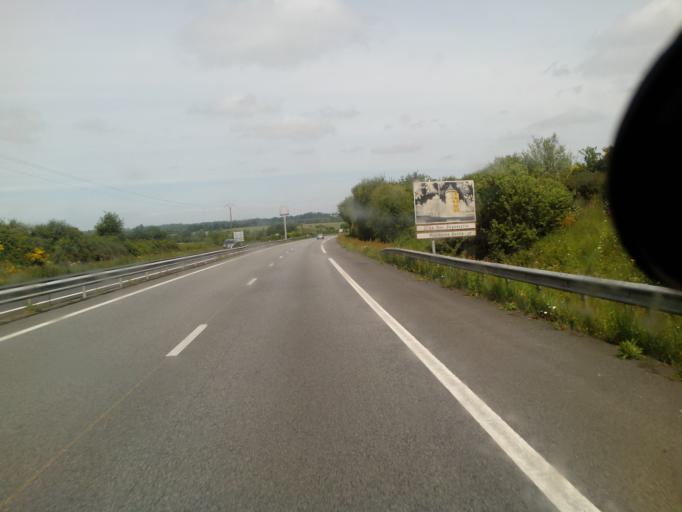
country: FR
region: Pays de la Loire
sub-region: Departement de la Loire-Atlantique
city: Derval
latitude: 47.6920
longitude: -1.7022
